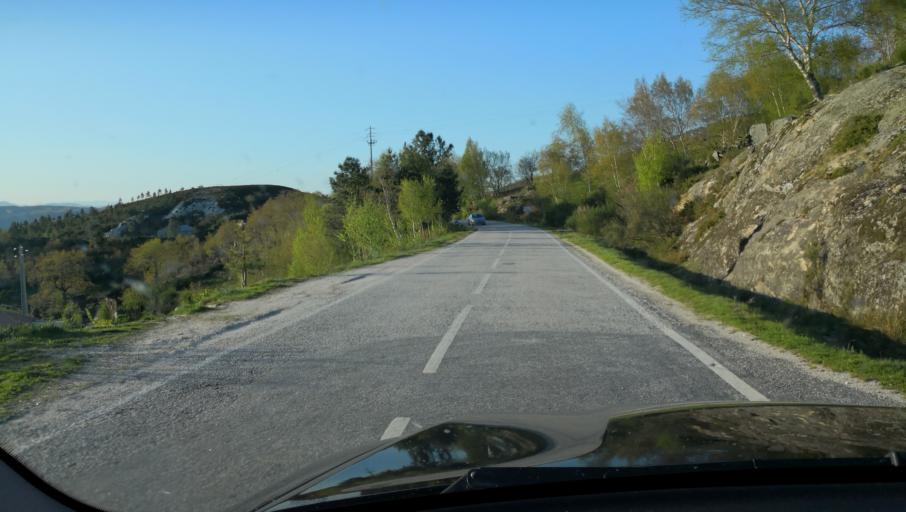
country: PT
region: Vila Real
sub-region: Vila Real
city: Vila Real
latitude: 41.3929
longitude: -7.8267
